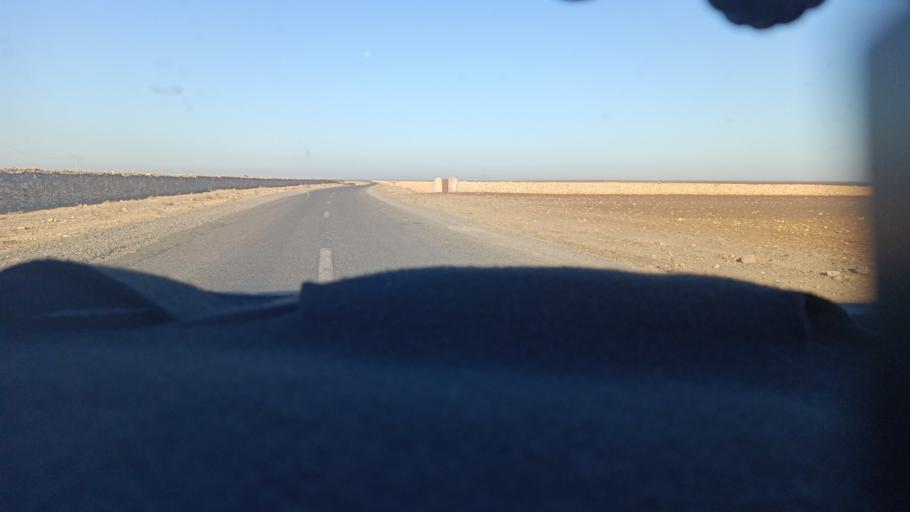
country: MA
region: Doukkala-Abda
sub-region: Safi
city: Youssoufia
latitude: 32.3714
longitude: -8.6925
